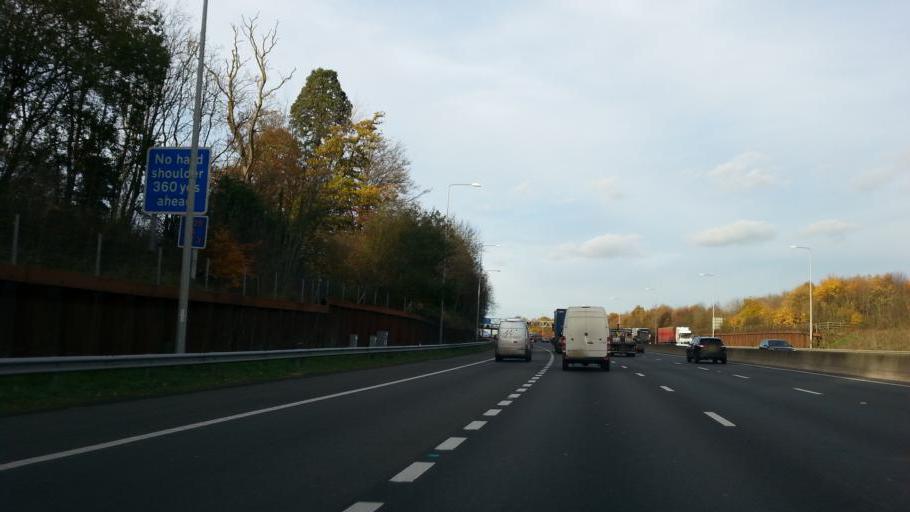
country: GB
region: England
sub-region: Hertfordshire
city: Kings Langley
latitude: 51.6861
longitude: -0.4475
